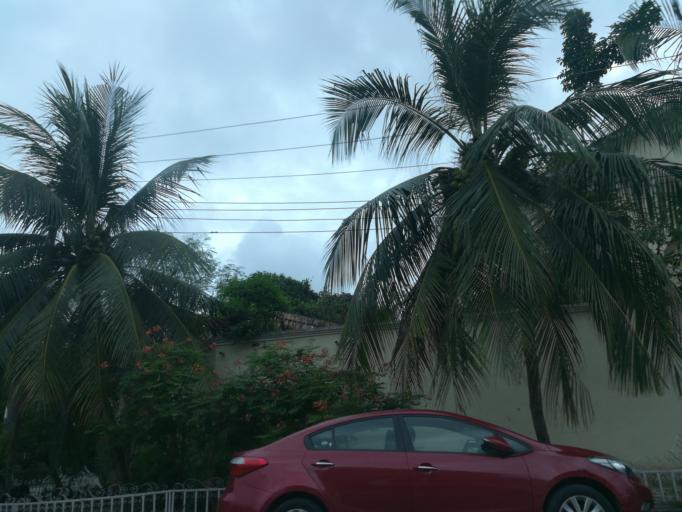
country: NG
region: Lagos
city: Ikoyi
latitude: 6.4472
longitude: 3.4560
